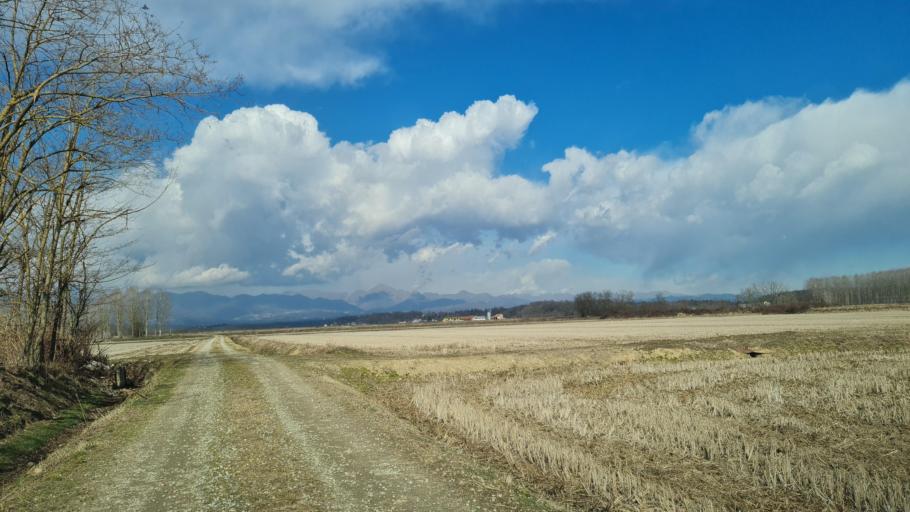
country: IT
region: Piedmont
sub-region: Provincia di Vercelli
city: Buronzo
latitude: 45.4826
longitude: 8.2536
